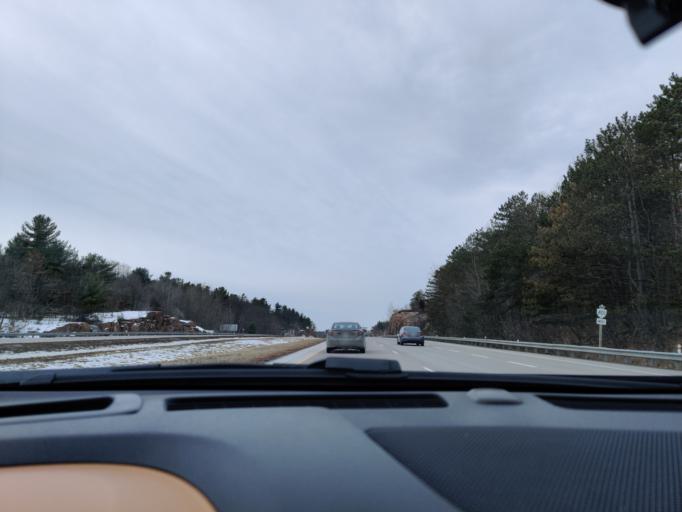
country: US
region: New York
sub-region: Jefferson County
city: Alexandria Bay
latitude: 44.3781
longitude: -76.0112
